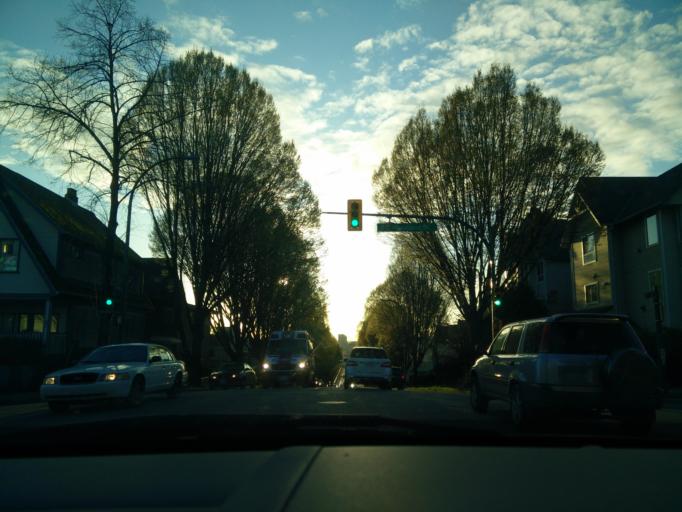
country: CA
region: British Columbia
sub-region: Fraser Valley Regional District
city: North Vancouver
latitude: 49.2697
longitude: -123.0733
